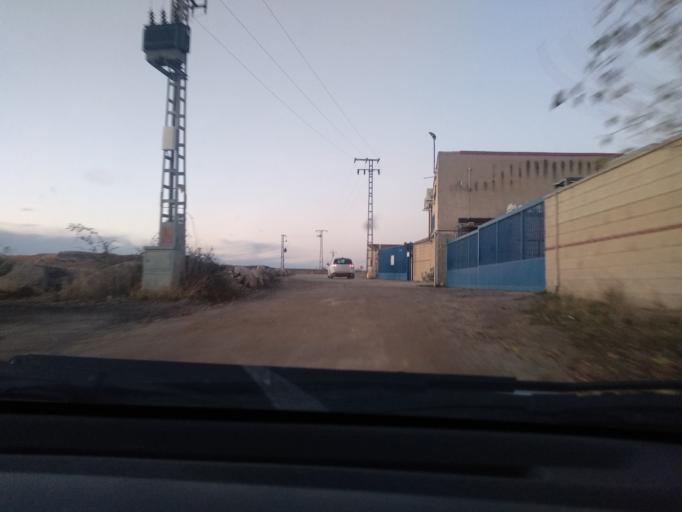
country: ES
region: Castille and Leon
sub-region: Provincia de Segovia
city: San Cristobal de Segovia
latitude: 40.9713
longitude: -4.0828
